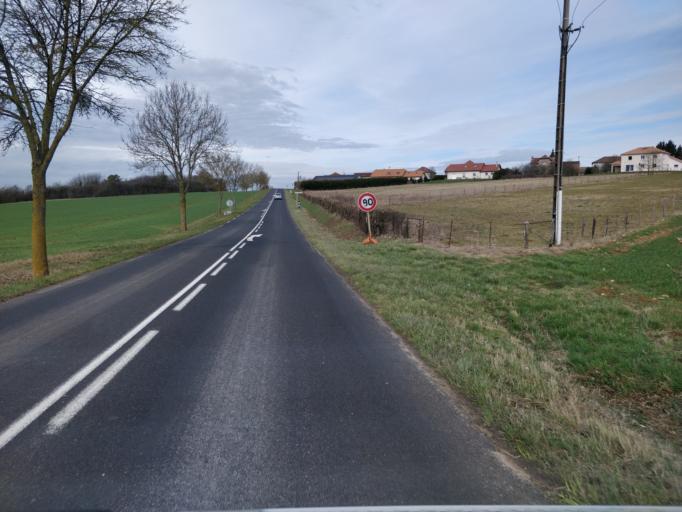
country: FR
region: Lorraine
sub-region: Departement de Meurthe-et-Moselle
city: Montauville
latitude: 48.9001
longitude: 5.9617
